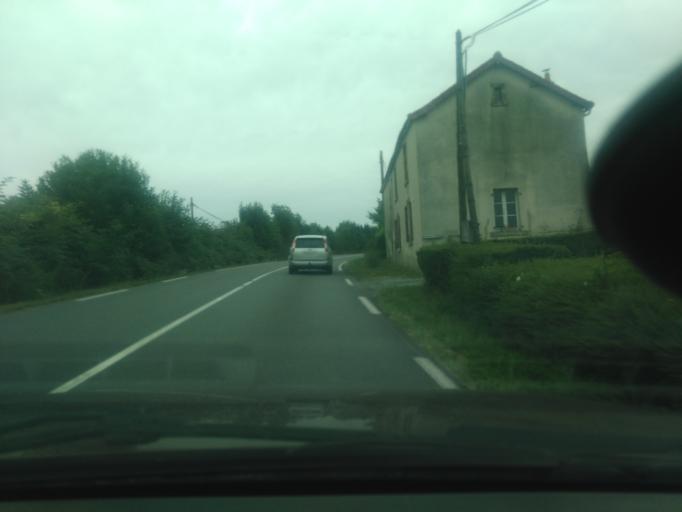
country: FR
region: Pays de la Loire
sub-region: Departement de la Vendee
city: Saint-Pierre-du-Chemin
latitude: 46.6515
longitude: -0.6630
